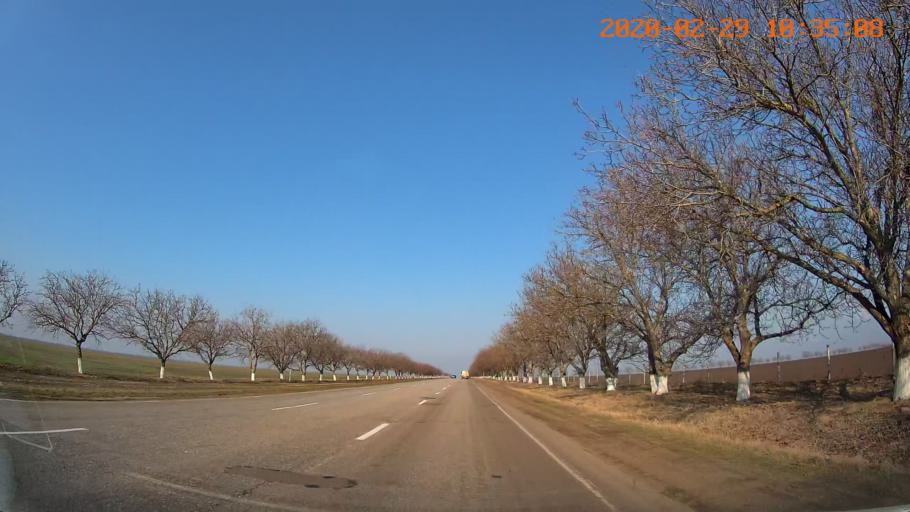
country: MD
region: Anenii Noi
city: Varnita
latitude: 46.9827
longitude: 29.5251
